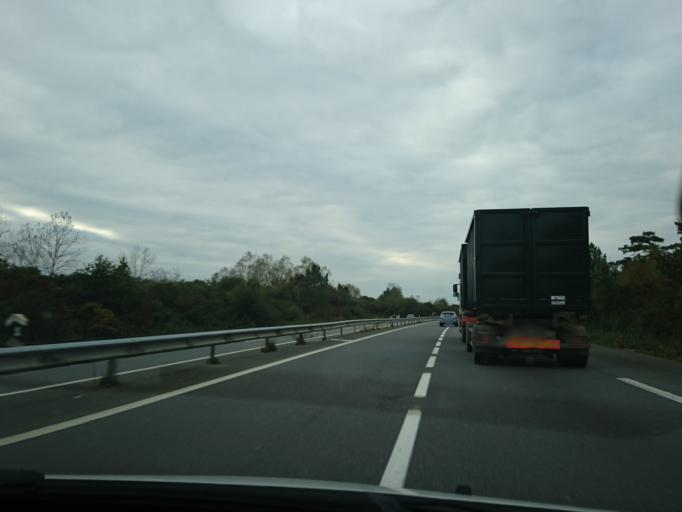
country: FR
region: Pays de la Loire
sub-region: Departement de la Loire-Atlantique
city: Pontchateau
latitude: 47.4201
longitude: -2.0490
